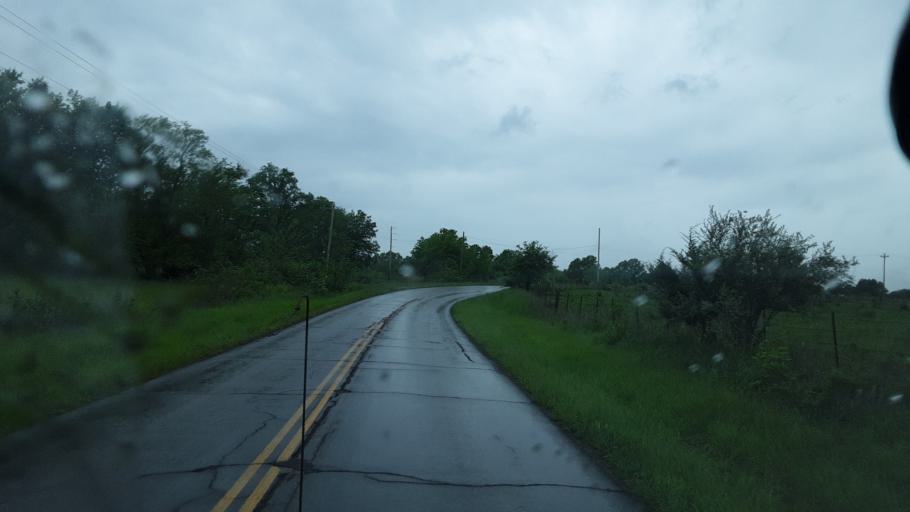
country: US
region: Missouri
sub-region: Boone County
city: Centralia
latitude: 39.3888
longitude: -92.2323
